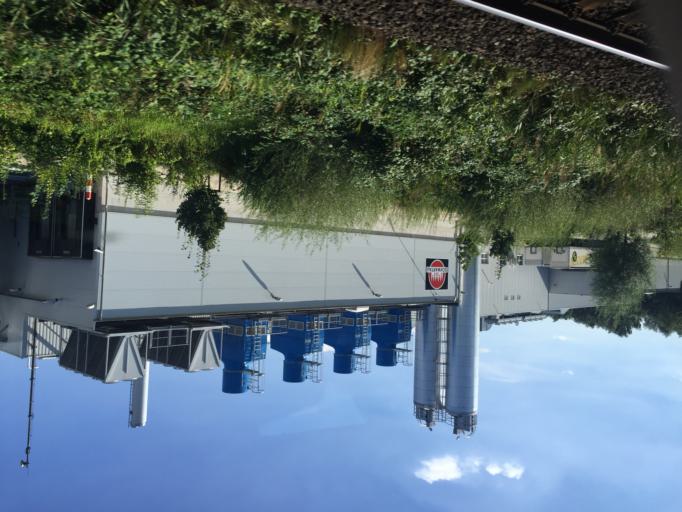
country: DE
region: Schleswig-Holstein
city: Bad Schwartau
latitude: 53.9033
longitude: 10.6921
